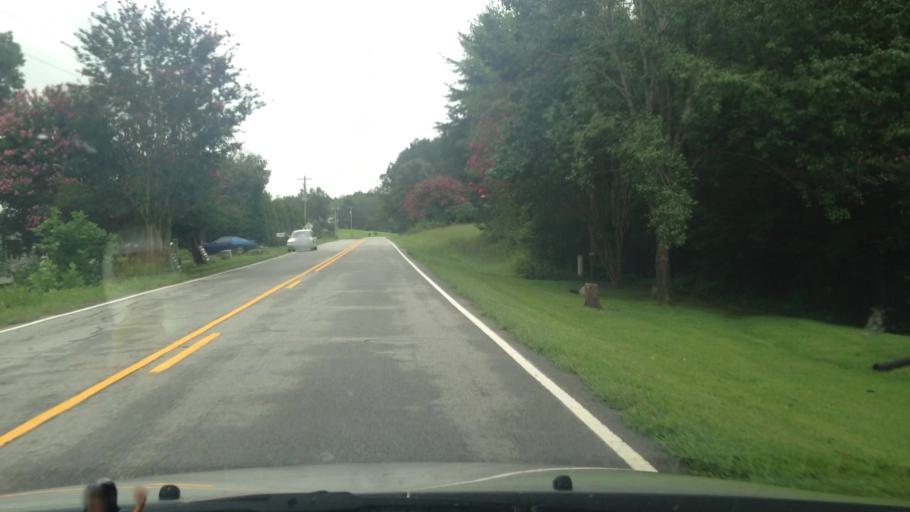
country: US
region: North Carolina
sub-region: Stokes County
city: Danbury
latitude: 36.4136
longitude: -80.1125
